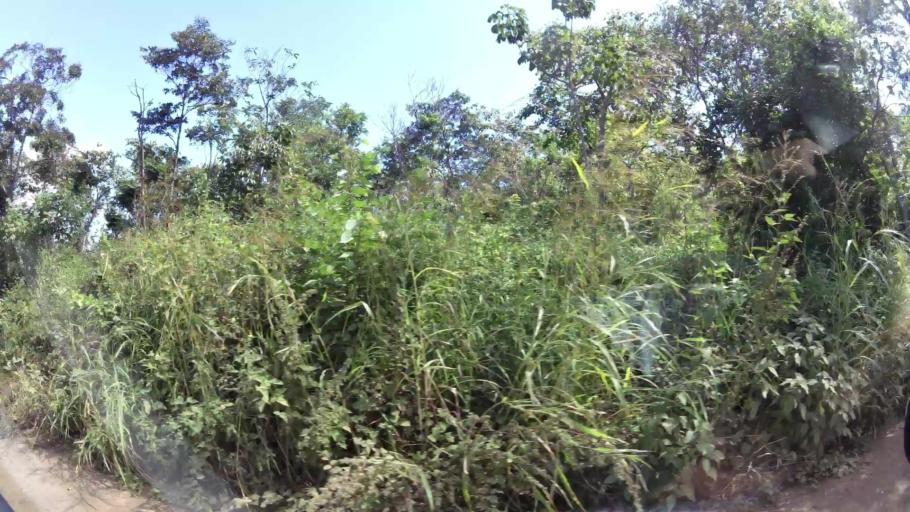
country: CR
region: Guanacaste
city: Bagaces
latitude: 10.5281
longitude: -85.2956
